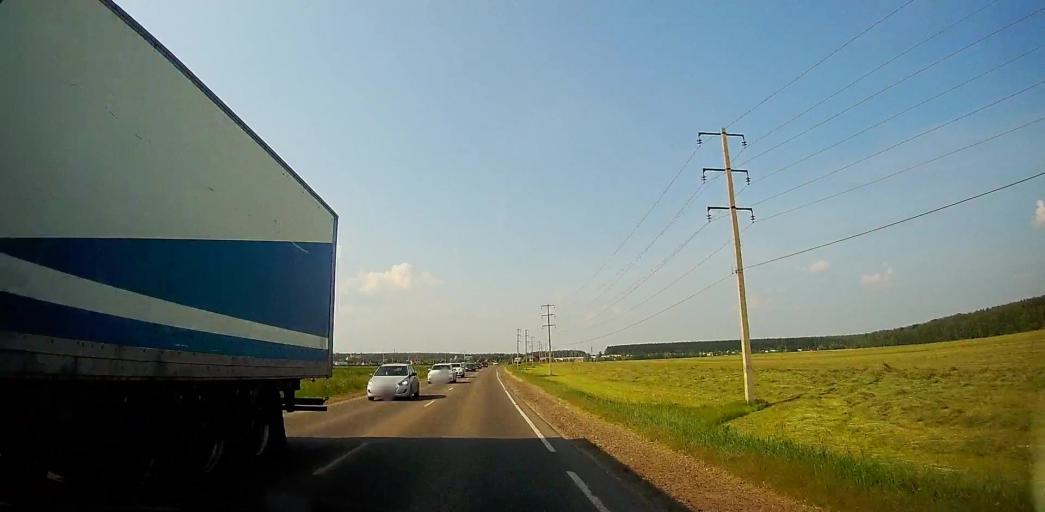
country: RU
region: Moskovskaya
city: Barybino
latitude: 55.2667
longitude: 37.9160
